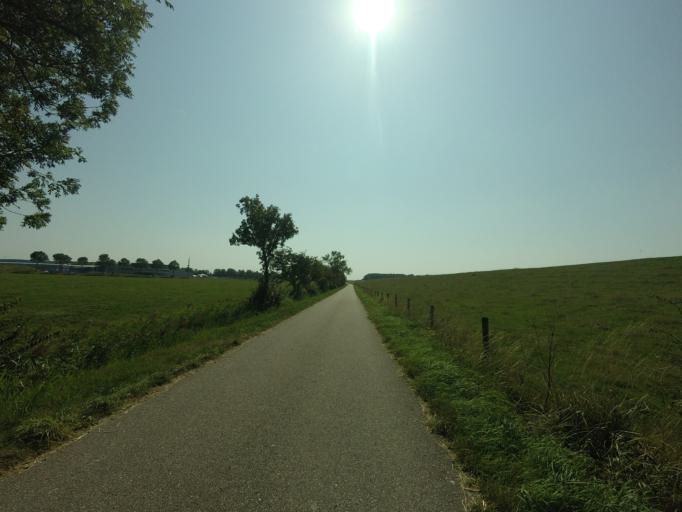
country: NL
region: Groningen
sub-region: Gemeente De Marne
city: Ulrum
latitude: 53.3479
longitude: 6.2970
